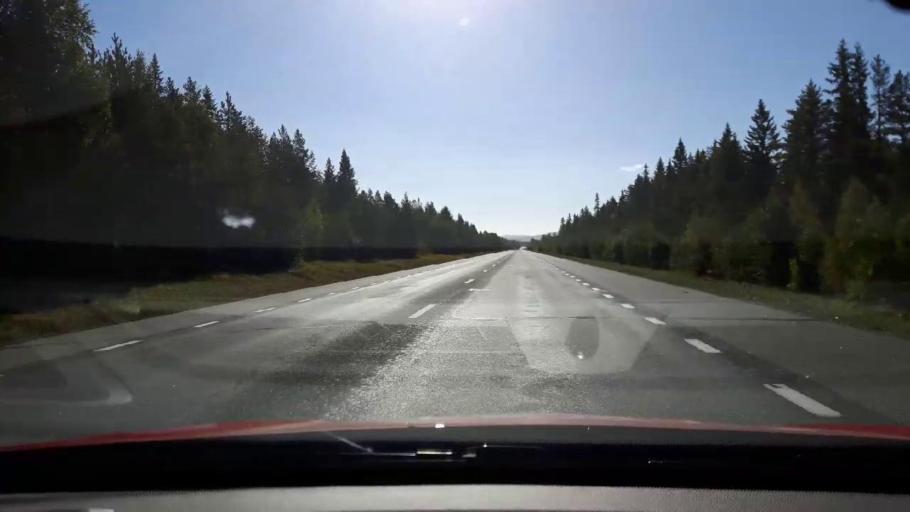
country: SE
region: Vaesternorrland
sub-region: Ange Kommun
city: Ange
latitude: 62.5895
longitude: 15.7167
